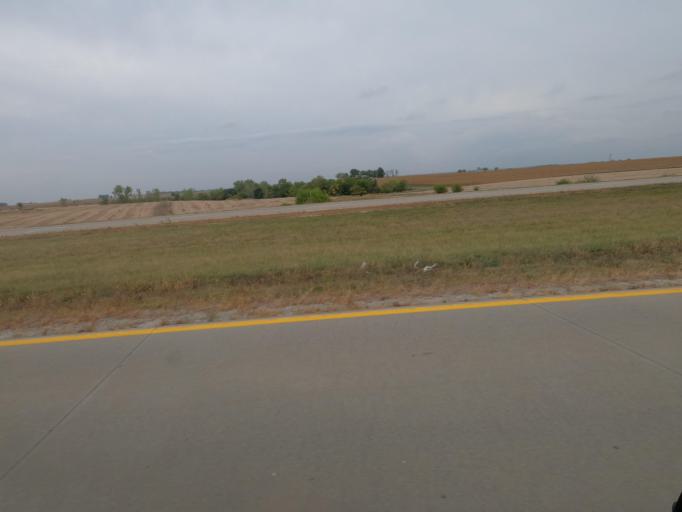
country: US
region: Iowa
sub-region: Marion County
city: Pella
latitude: 41.3603
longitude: -92.7772
